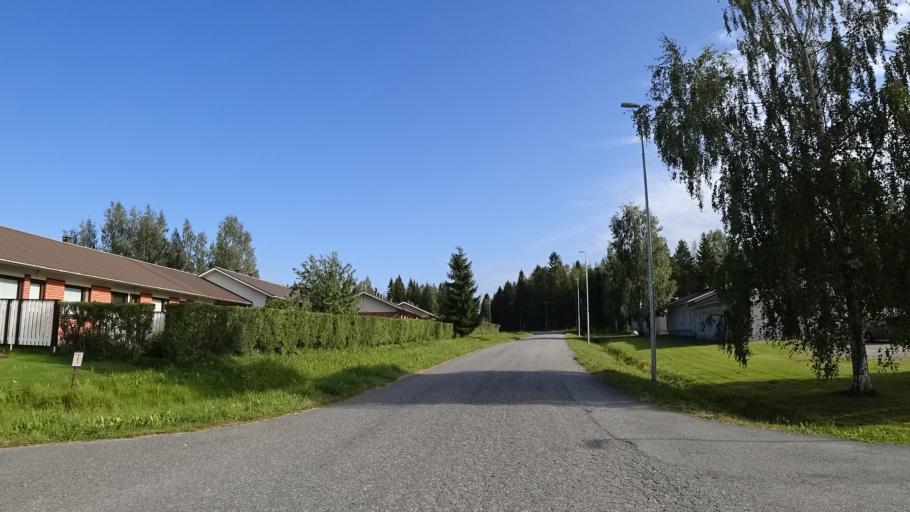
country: FI
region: North Karelia
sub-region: Joensuu
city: Eno
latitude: 62.7944
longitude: 30.1409
